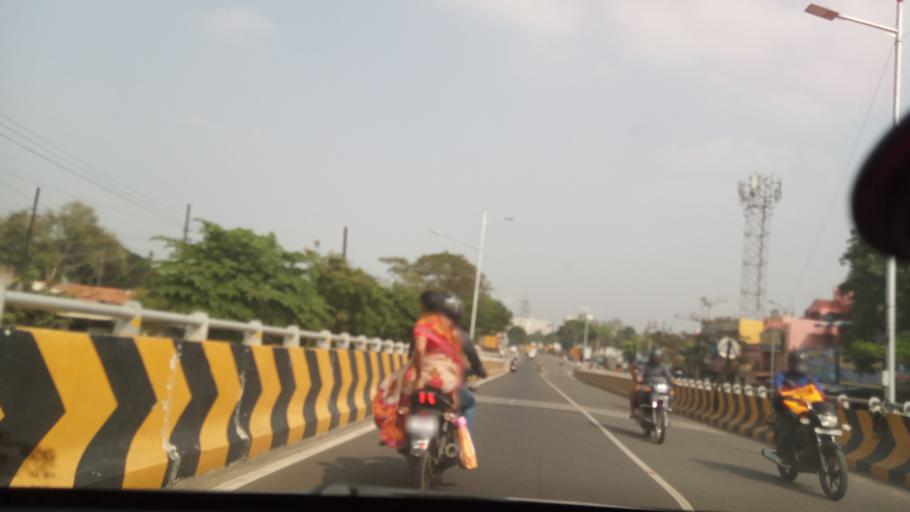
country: IN
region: Tamil Nadu
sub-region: Coimbatore
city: Coimbatore
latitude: 11.0213
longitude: 76.9809
